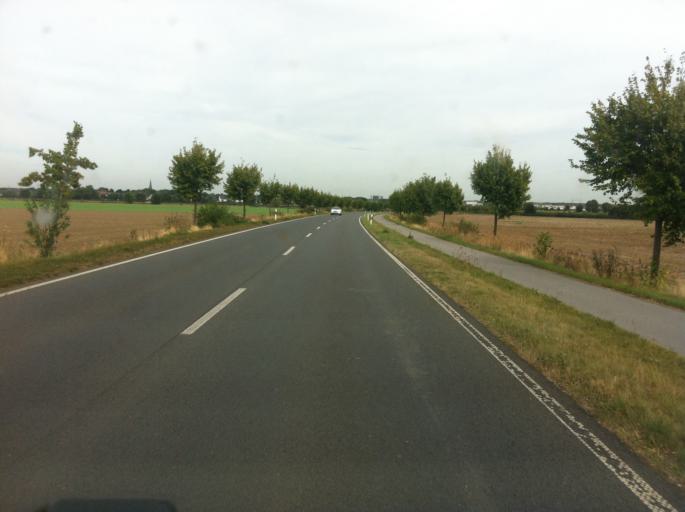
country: DE
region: North Rhine-Westphalia
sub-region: Regierungsbezirk Koln
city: Frechen
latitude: 50.9546
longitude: 6.8191
